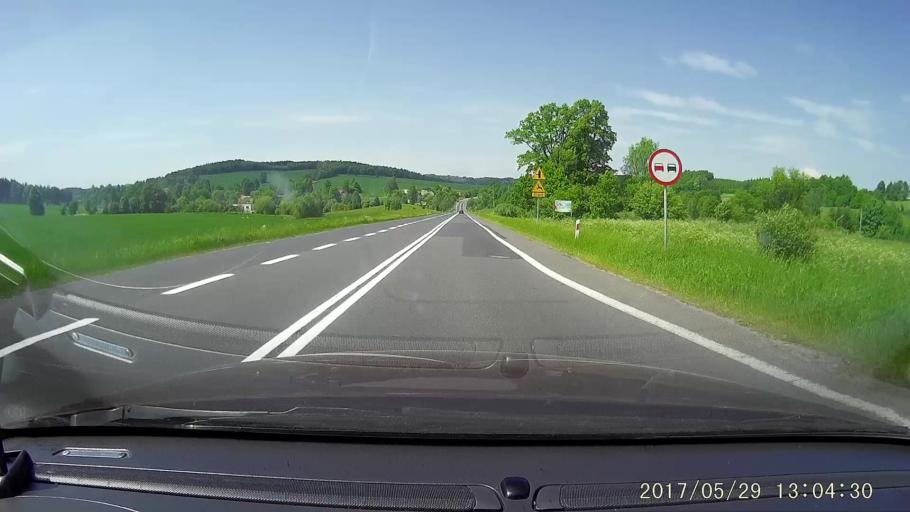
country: PL
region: Lower Silesian Voivodeship
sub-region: Powiat jeleniogorski
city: Stara Kamienica
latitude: 50.9337
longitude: 15.6014
